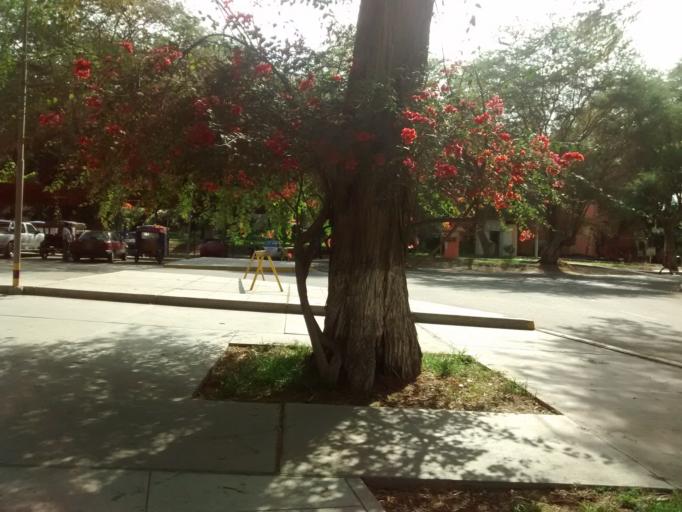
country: PE
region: Piura
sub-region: Provincia de Piura
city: Piura
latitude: -5.1796
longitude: -80.6191
